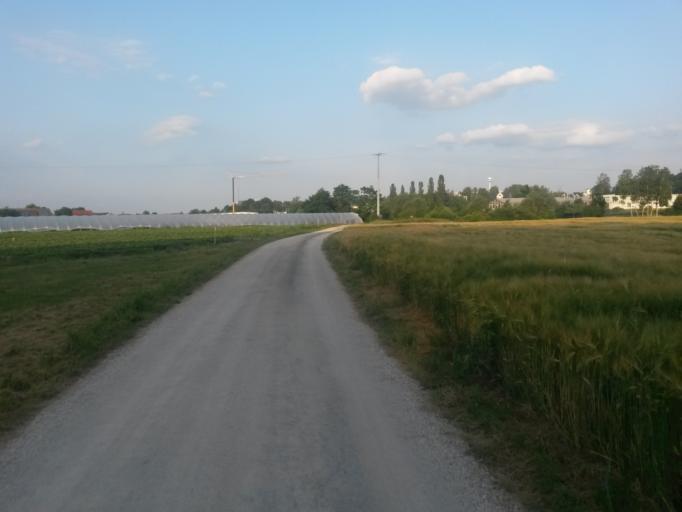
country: DE
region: Bavaria
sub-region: Regierungsbezirk Mittelfranken
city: Zirndorf
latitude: 49.4323
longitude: 10.9298
